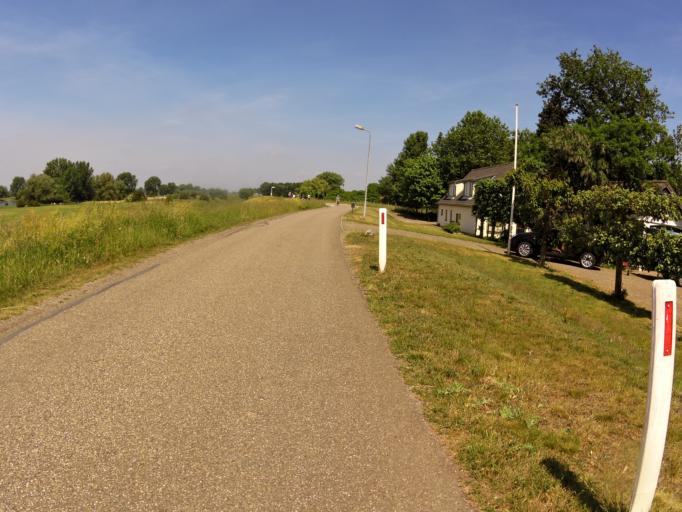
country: NL
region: Gelderland
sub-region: Gemeente Maasdriel
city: Heerewaarden
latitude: 51.7600
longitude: 5.3637
